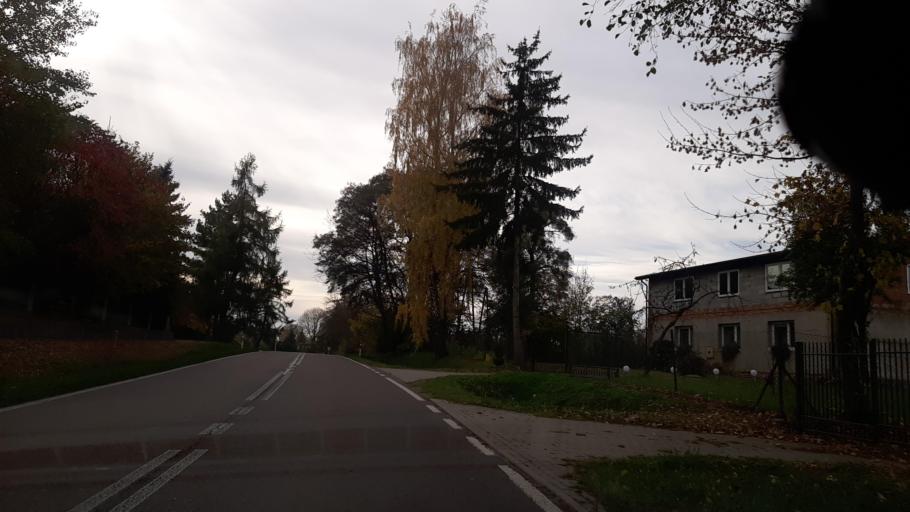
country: PL
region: Lublin Voivodeship
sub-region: Powiat pulawski
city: Naleczow
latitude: 51.3232
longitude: 22.2368
